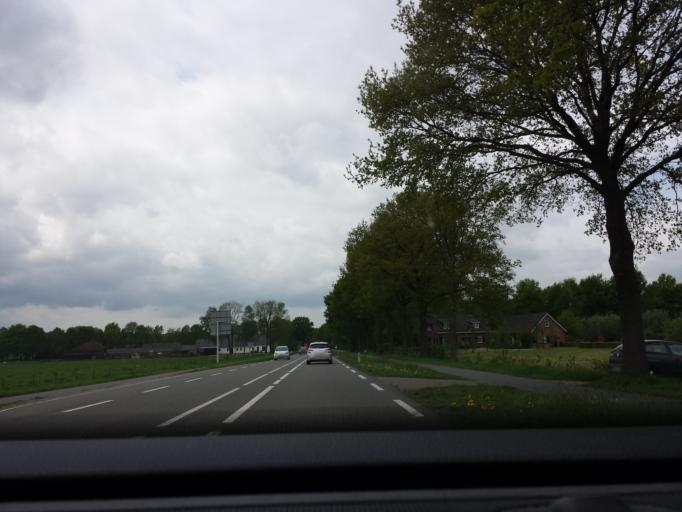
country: NL
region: Gelderland
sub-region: Gemeente Montferland
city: s-Heerenberg
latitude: 51.8991
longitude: 6.2723
